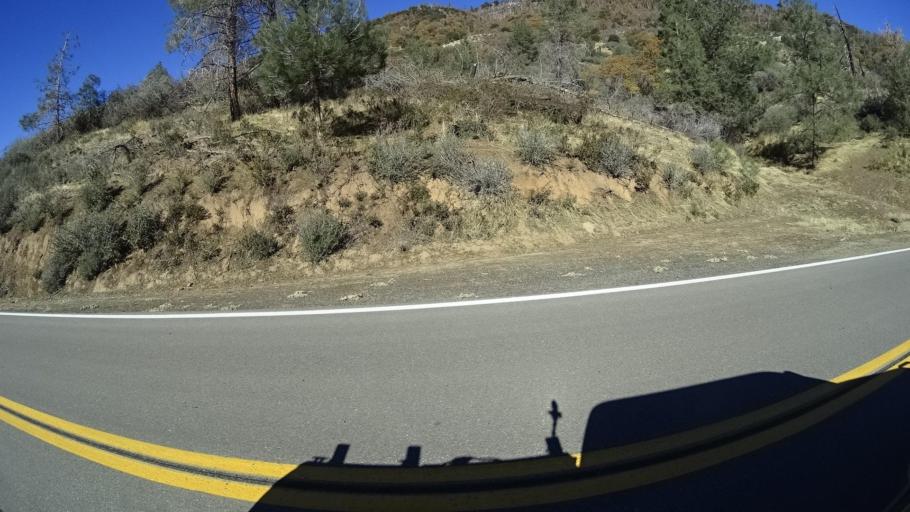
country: US
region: California
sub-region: Kern County
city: Alta Sierra
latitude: 35.7463
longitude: -118.5938
